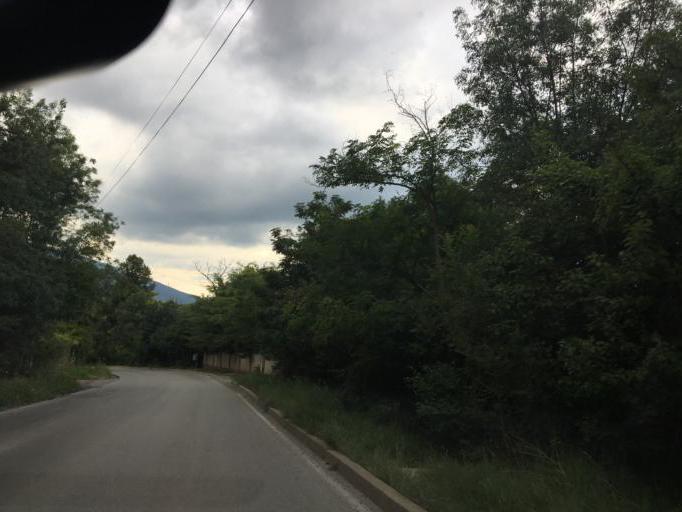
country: BG
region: Sofia-Capital
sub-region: Stolichna Obshtina
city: Sofia
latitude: 42.6177
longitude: 23.3601
